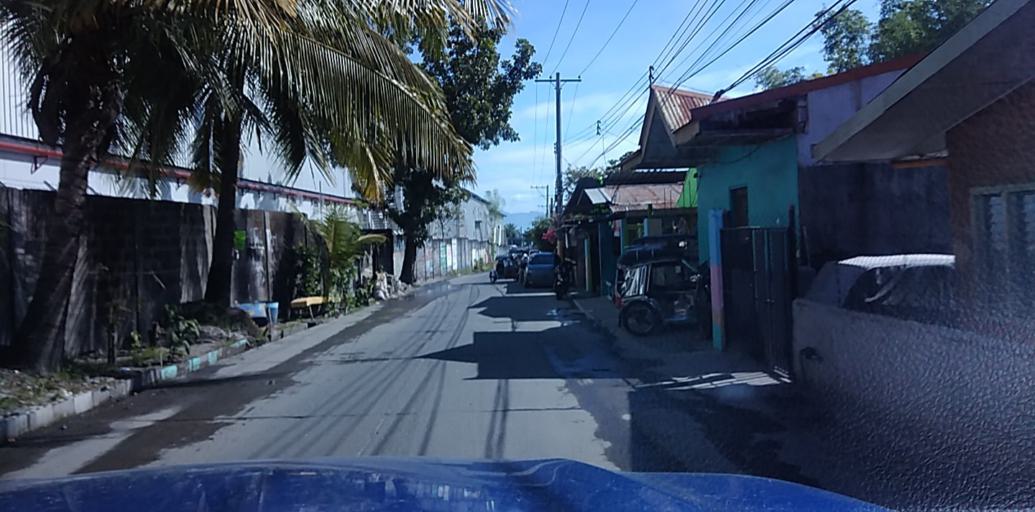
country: PH
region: Central Luzon
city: Santol
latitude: 15.1724
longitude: 120.5188
